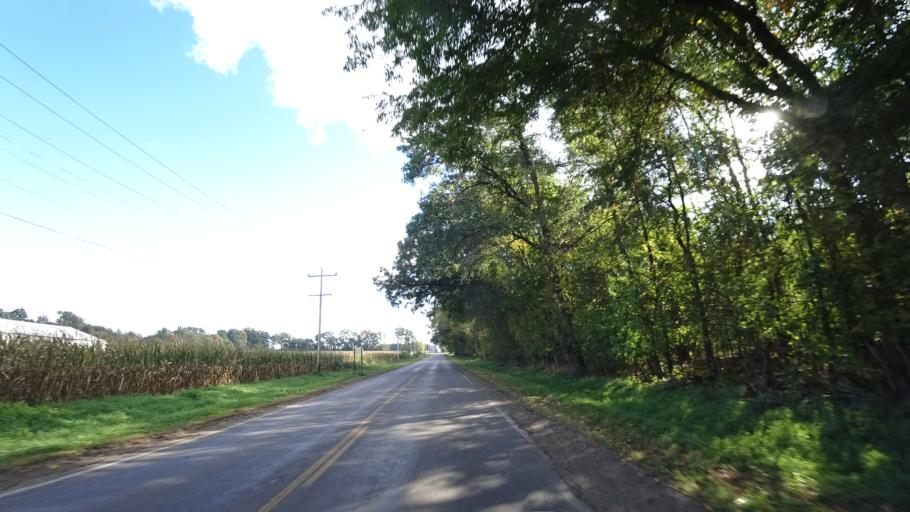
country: US
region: Michigan
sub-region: Saint Joseph County
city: Centreville
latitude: 41.9659
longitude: -85.5279
